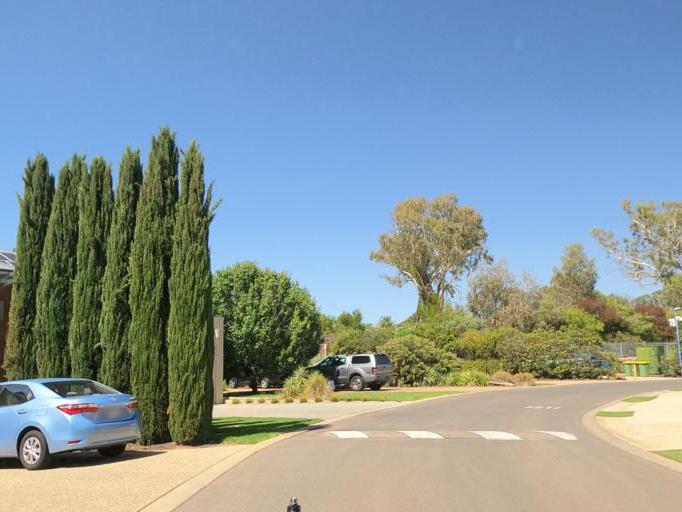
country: AU
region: New South Wales
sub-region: Corowa Shire
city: Mulwala
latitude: -36.0010
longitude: 146.0034
